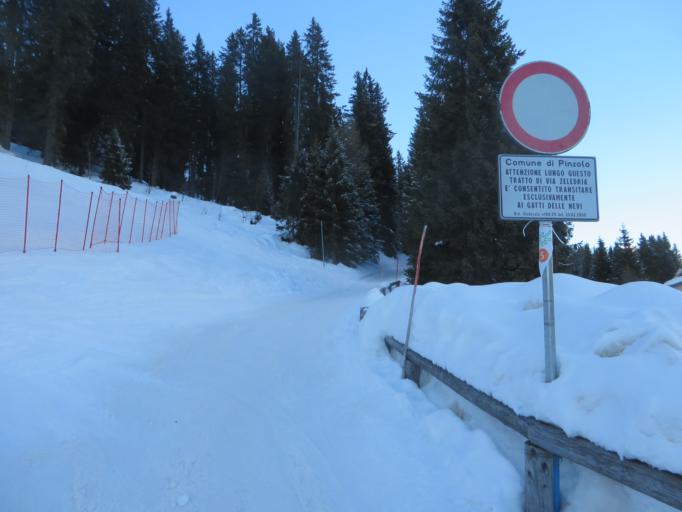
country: IT
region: Trentino-Alto Adige
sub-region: Provincia di Trento
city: Commezzadura
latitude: 46.2440
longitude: 10.8373
